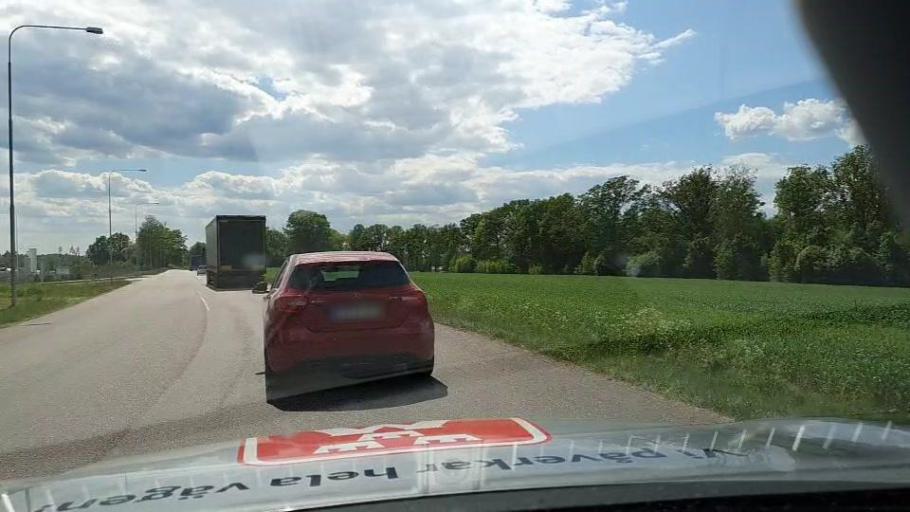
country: SE
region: Kronoberg
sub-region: Ljungby Kommun
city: Ljungby
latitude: 56.8579
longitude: 13.9385
